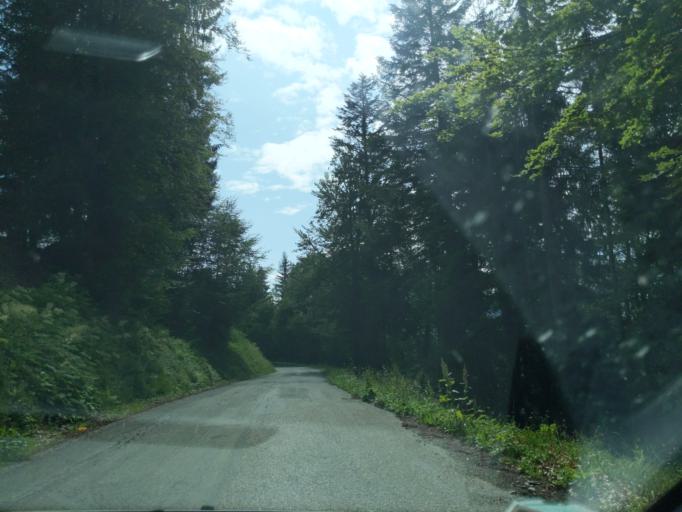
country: FR
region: Rhone-Alpes
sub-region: Departement de la Savoie
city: Ugine
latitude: 45.7506
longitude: 6.4726
